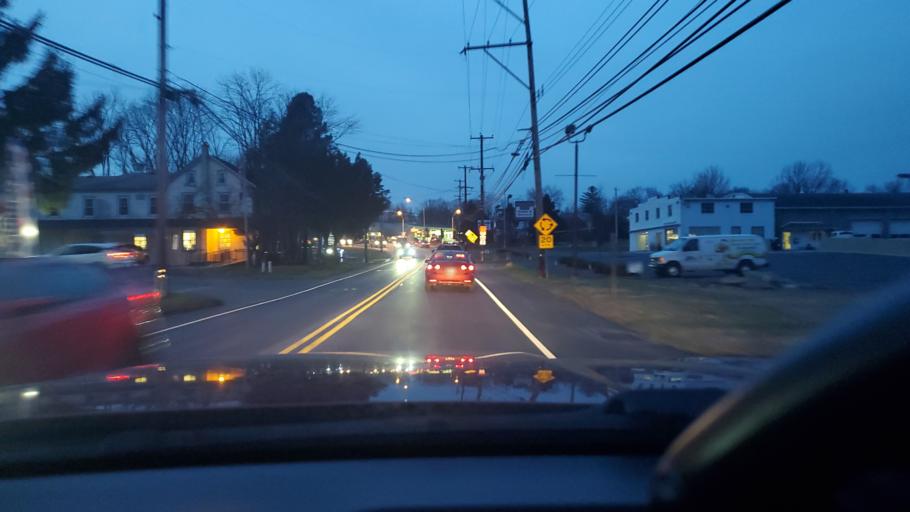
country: US
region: Pennsylvania
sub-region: Montgomery County
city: Spring Mount
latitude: 40.2763
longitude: -75.4783
